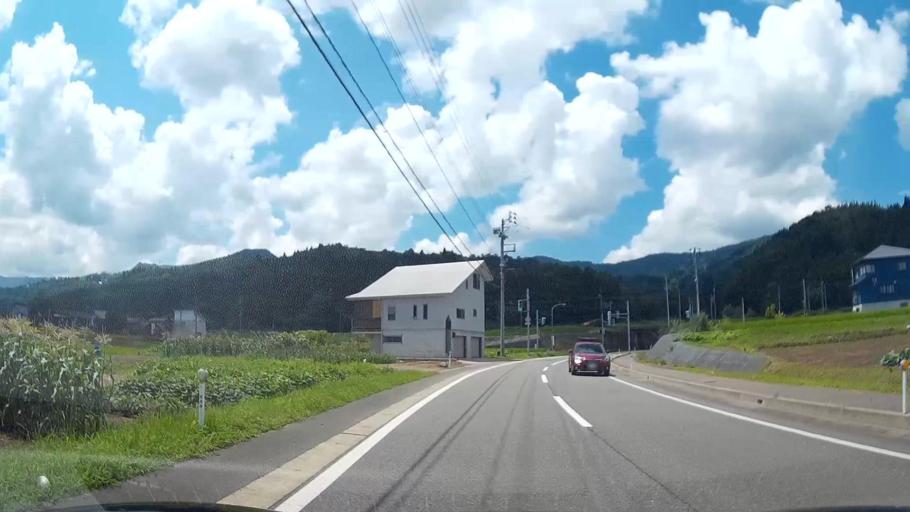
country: JP
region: Niigata
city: Shiozawa
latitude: 37.0179
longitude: 138.8210
